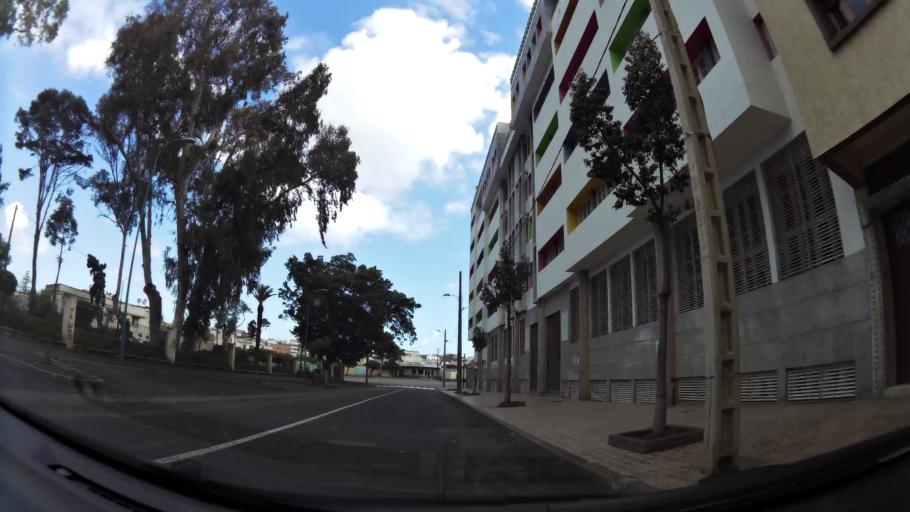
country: MA
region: Grand Casablanca
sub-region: Casablanca
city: Casablanca
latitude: 33.5663
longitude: -7.6113
